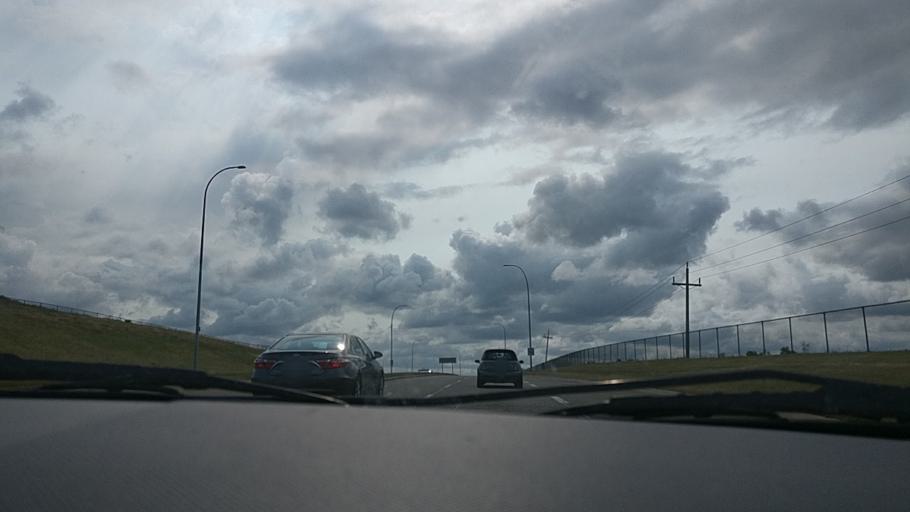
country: CA
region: Alberta
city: Calgary
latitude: 51.0959
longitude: -114.1151
